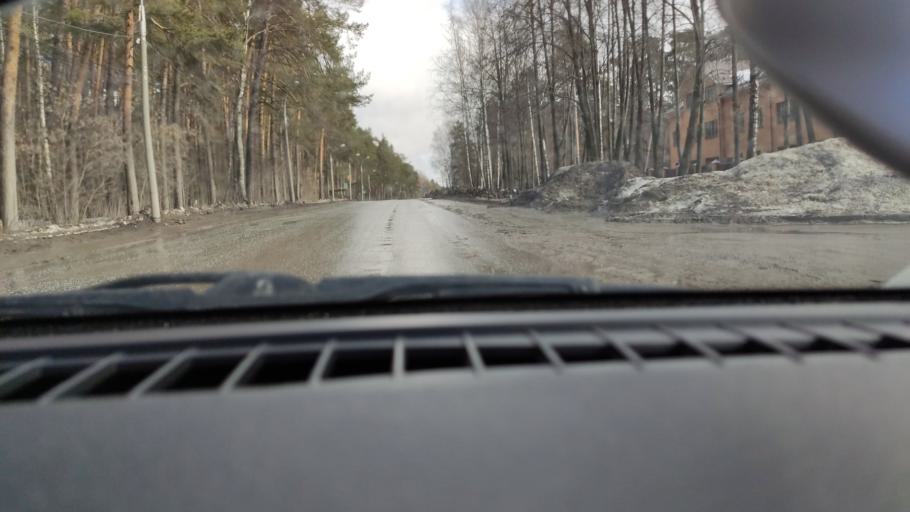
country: RU
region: Perm
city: Kondratovo
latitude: 58.0139
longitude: 55.9945
